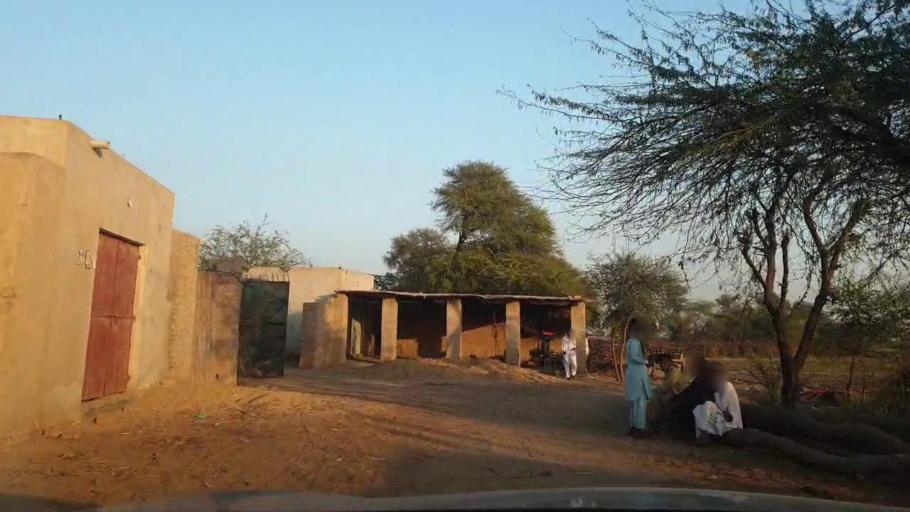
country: PK
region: Sindh
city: Berani
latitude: 25.6719
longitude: 68.7637
